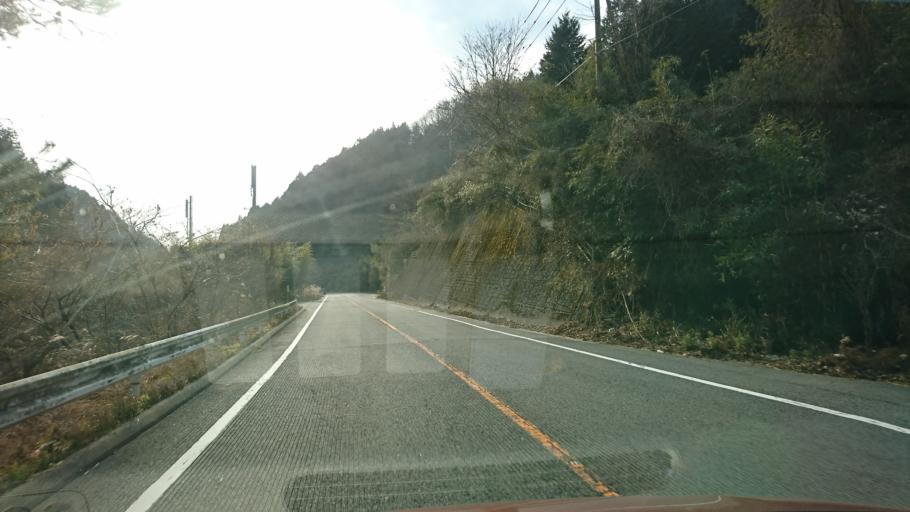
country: JP
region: Ehime
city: Hojo
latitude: 33.9302
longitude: 132.8964
